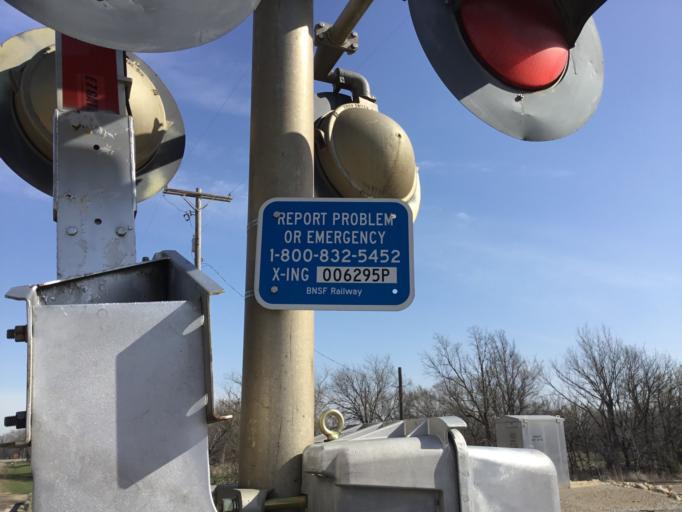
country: US
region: Kansas
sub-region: Lyon County
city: Emporia
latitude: 38.3737
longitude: -95.9926
